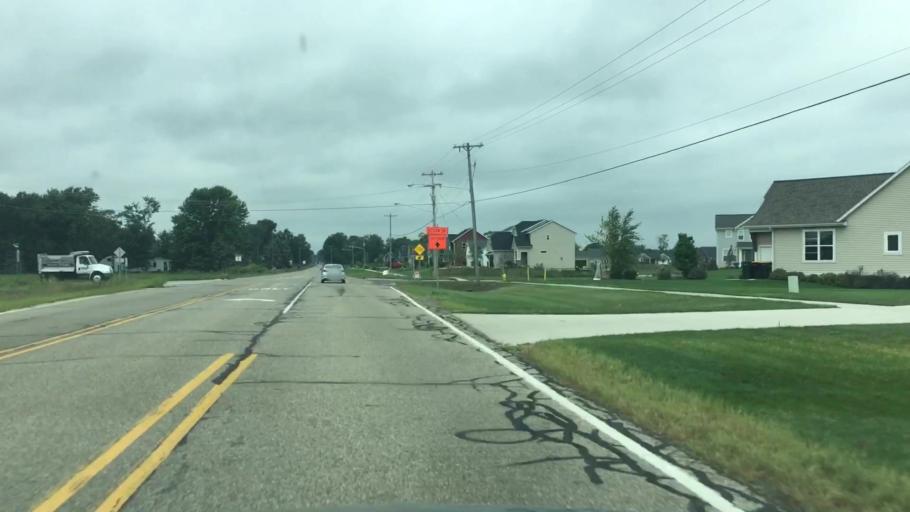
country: US
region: Michigan
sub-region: Ottawa County
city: Hudsonville
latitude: 42.8709
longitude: -85.8355
